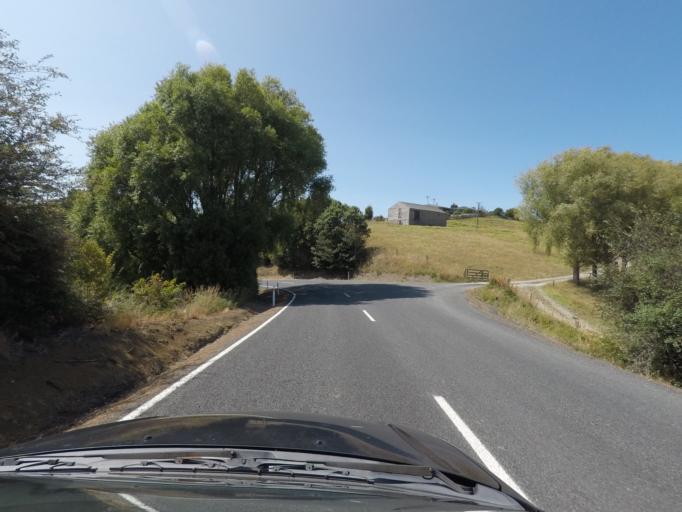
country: NZ
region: Auckland
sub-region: Auckland
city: Warkworth
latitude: -36.4500
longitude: 174.7562
